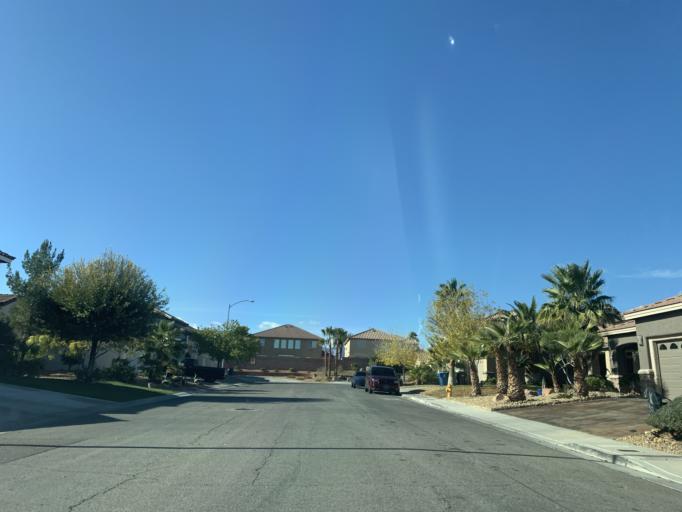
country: US
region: Nevada
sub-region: Clark County
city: Summerlin South
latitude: 36.1194
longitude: -115.2911
